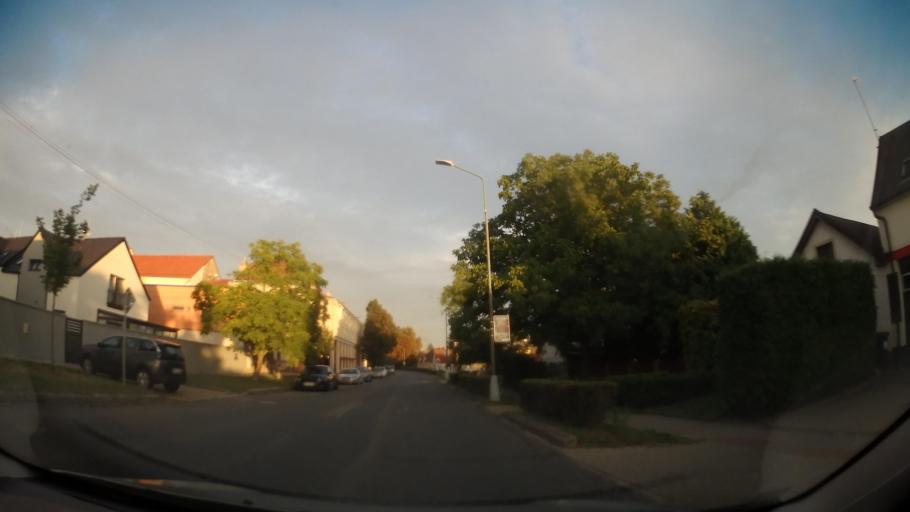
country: CZ
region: Central Bohemia
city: Milovice
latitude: 50.2265
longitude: 14.8873
